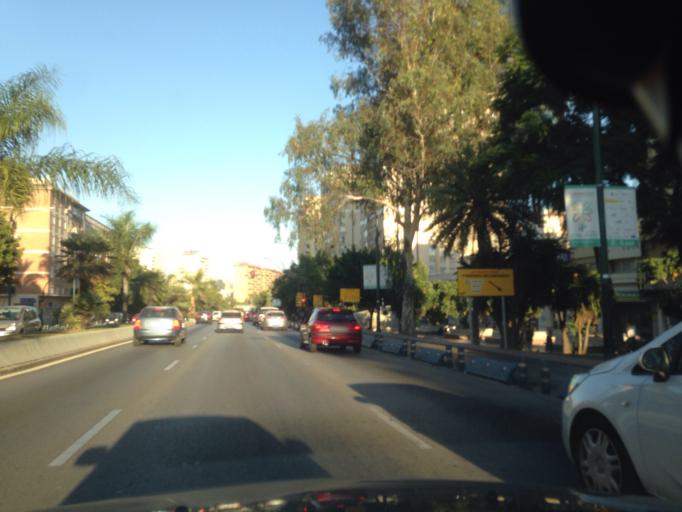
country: ES
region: Andalusia
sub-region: Provincia de Malaga
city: Malaga
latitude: 36.7163
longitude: -4.4412
